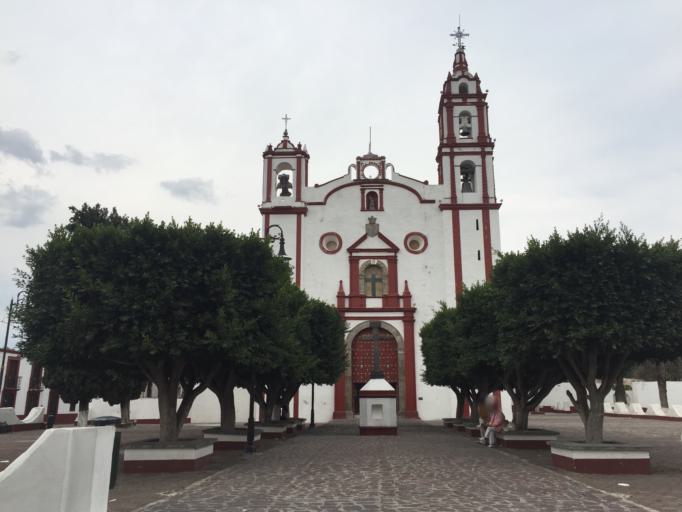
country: MX
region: Puebla
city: Tecali de Herrera
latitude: 18.9008
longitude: -97.9693
